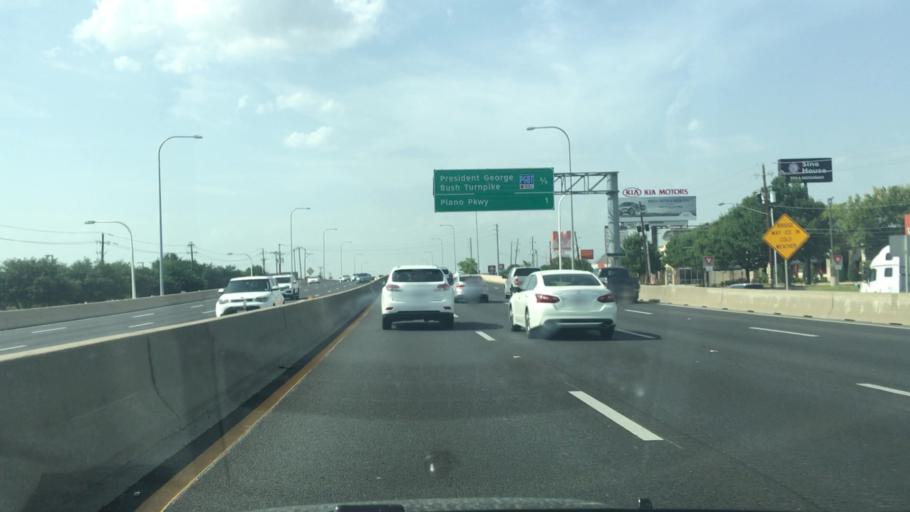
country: US
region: Texas
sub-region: Dallas County
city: Addison
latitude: 32.9947
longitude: -96.8293
